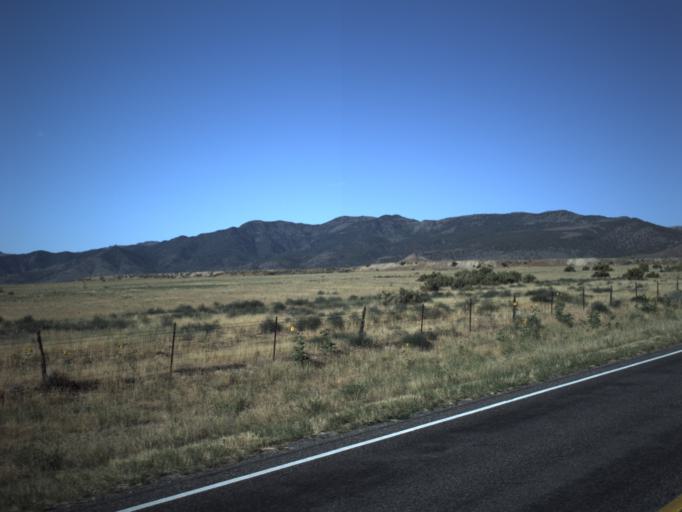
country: US
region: Utah
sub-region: Utah County
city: Genola
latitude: 39.9518
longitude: -111.9733
